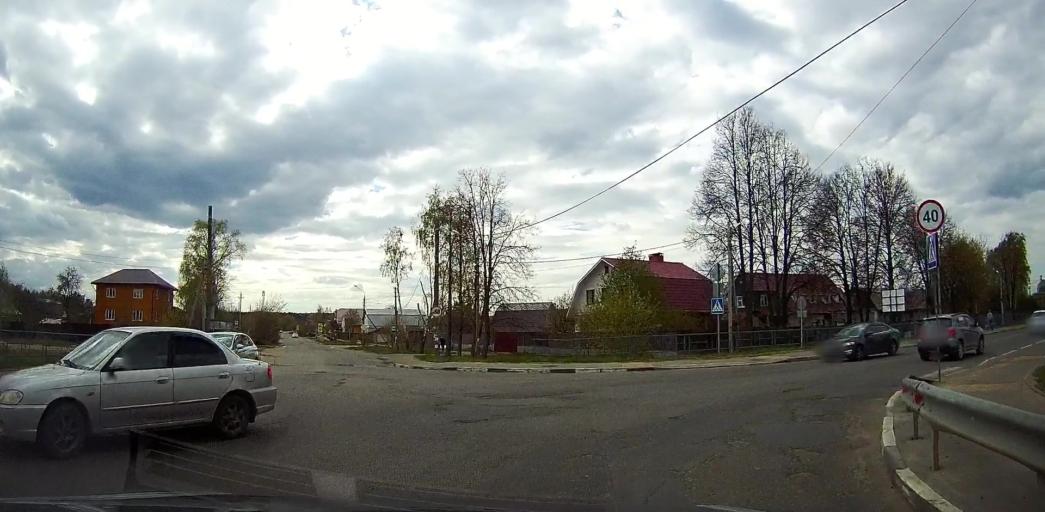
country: RU
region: Moskovskaya
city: Pavlovskiy Posad
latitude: 55.7699
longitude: 38.6449
